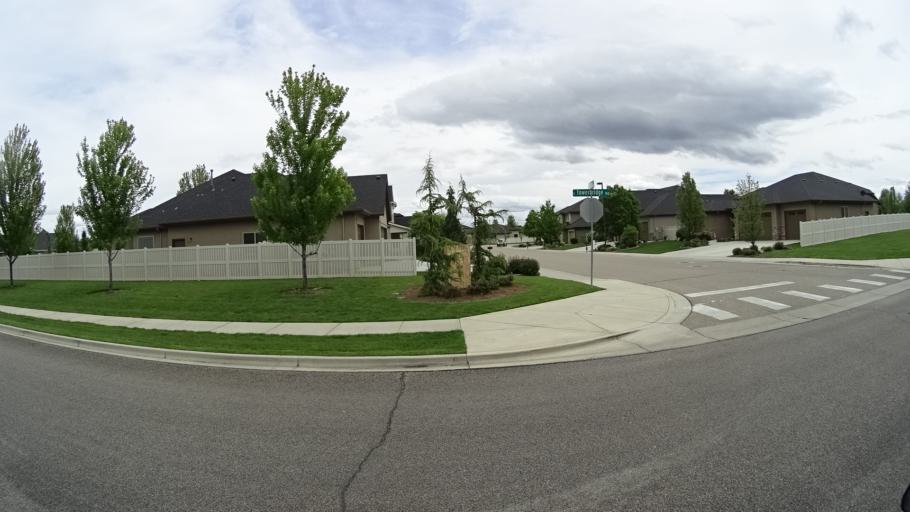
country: US
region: Idaho
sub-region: Ada County
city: Meridian
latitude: 43.6410
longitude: -116.4240
